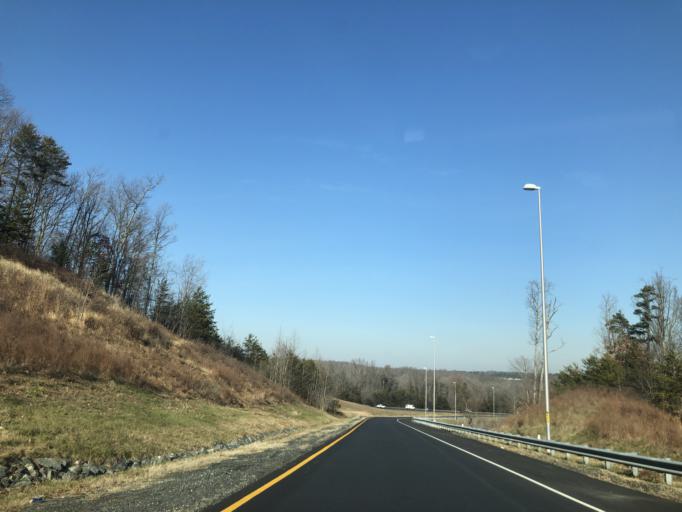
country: US
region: Virginia
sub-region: Stafford County
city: Falmouth
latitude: 38.3742
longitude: -77.4585
